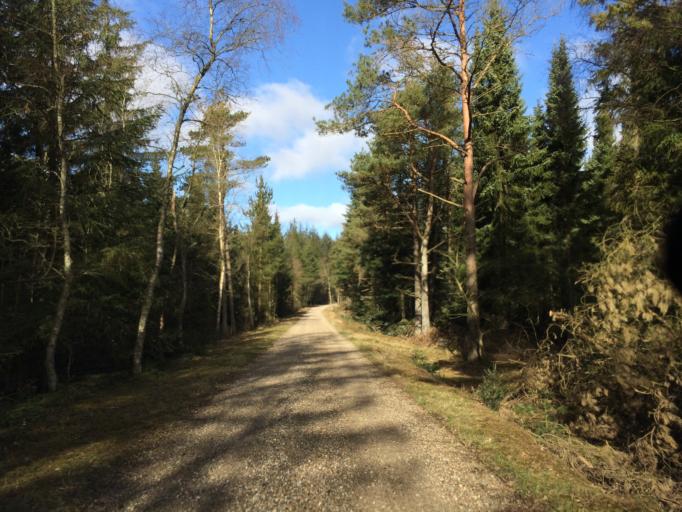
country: DK
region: Central Jutland
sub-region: Holstebro Kommune
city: Ulfborg
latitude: 56.2741
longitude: 8.4272
